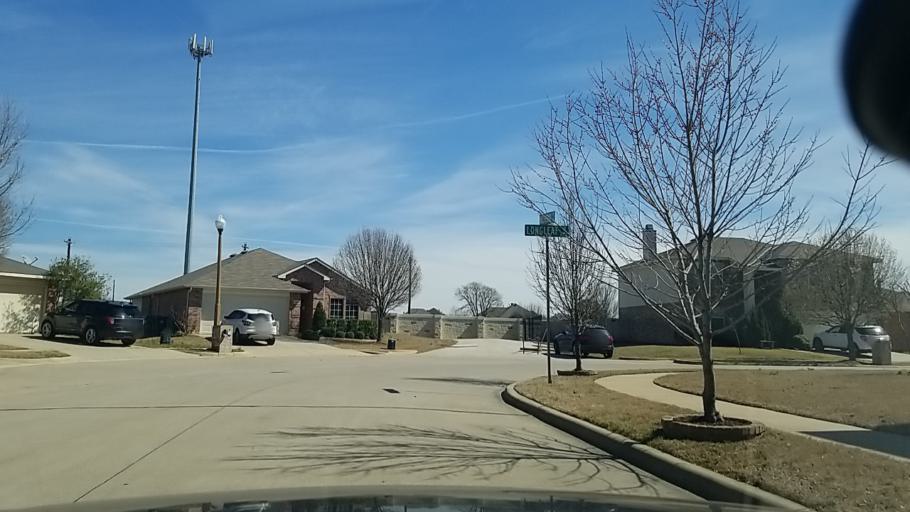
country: US
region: Texas
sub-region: Denton County
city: Corinth
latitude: 33.1499
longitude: -97.0985
